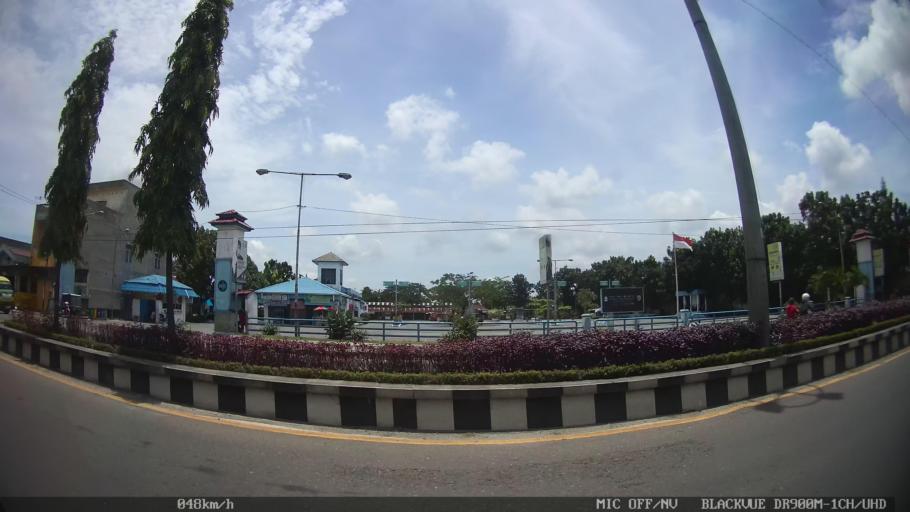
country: ID
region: North Sumatra
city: Percut
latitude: 3.5543
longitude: 98.8748
